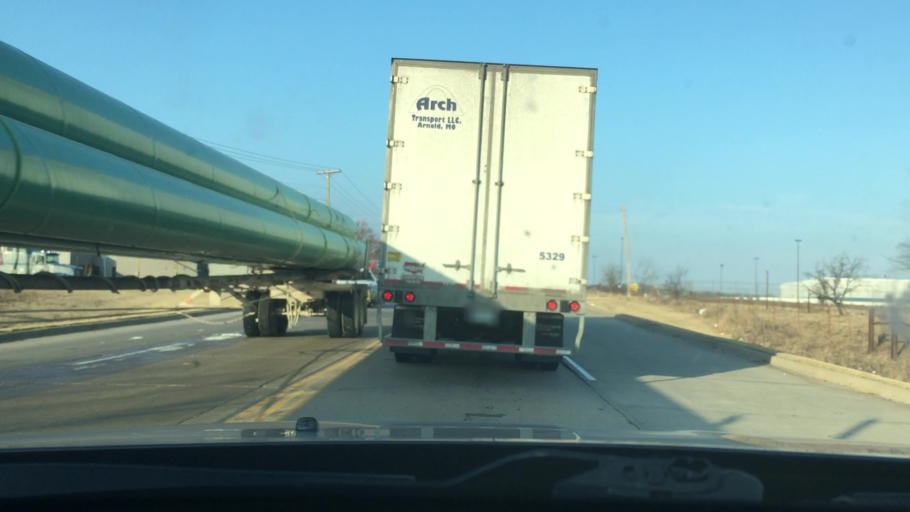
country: US
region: Oklahoma
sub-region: Carter County
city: Ardmore
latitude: 34.2020
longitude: -97.1678
